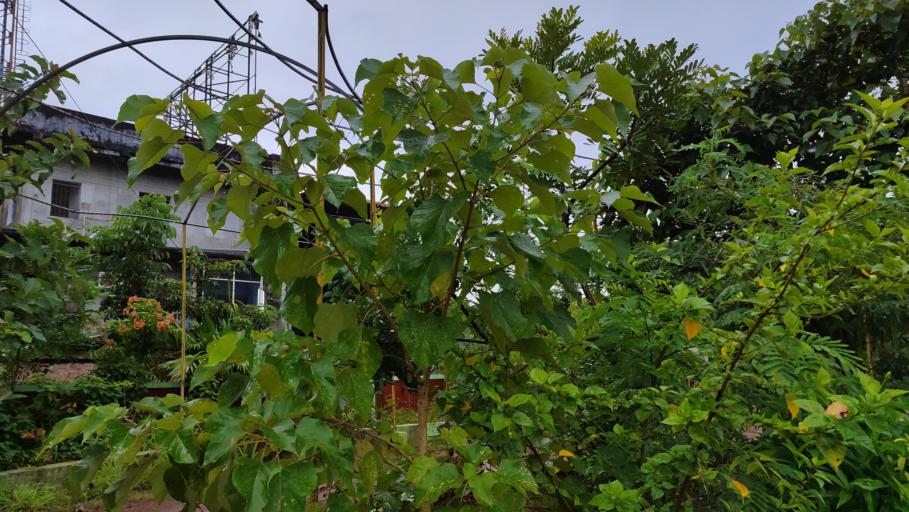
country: IN
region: Kerala
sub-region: Kasaragod District
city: Nileshwar
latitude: 12.1938
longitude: 75.1650
